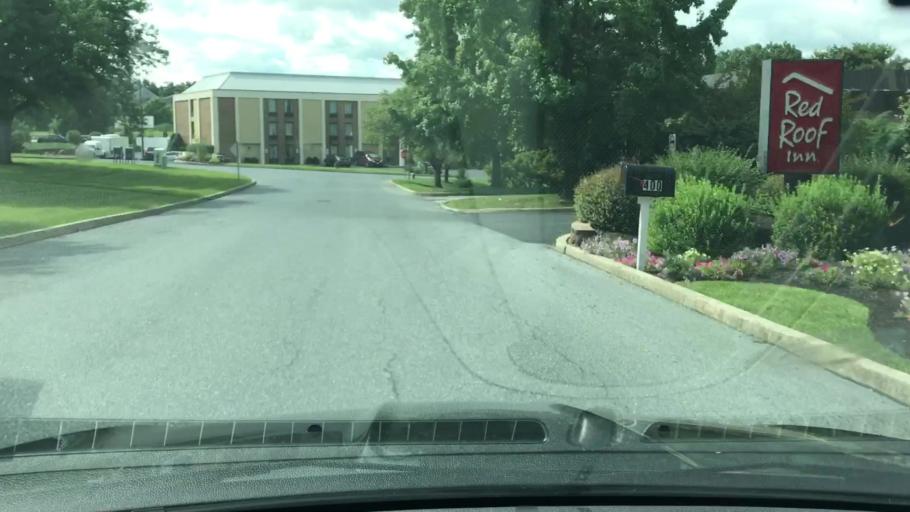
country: US
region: Pennsylvania
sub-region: Dauphin County
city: Progress
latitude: 40.3062
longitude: -76.8482
